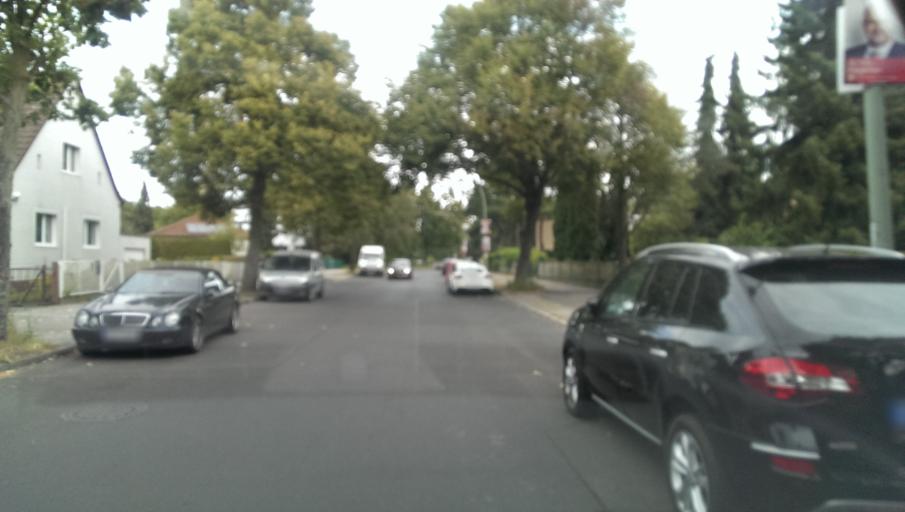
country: DE
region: Berlin
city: Britz
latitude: 52.4231
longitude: 13.4277
